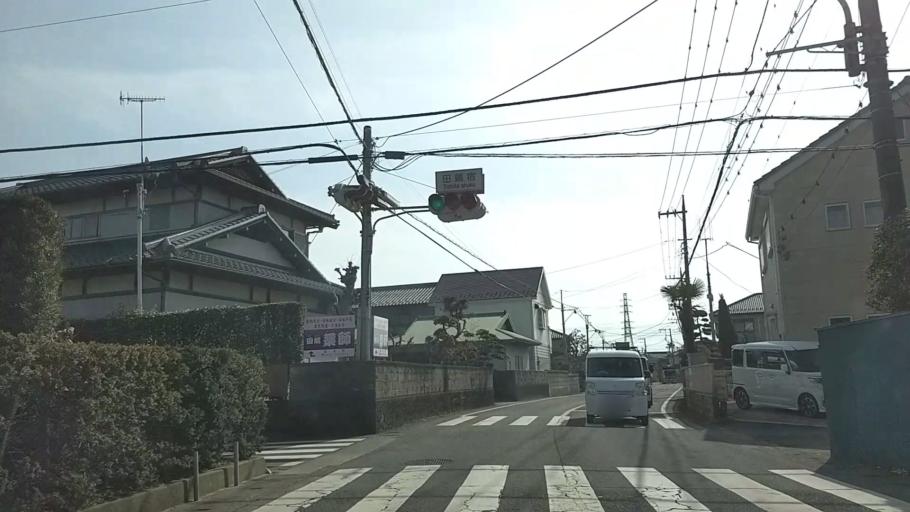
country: JP
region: Kanagawa
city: Chigasaki
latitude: 35.3550
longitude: 139.3848
